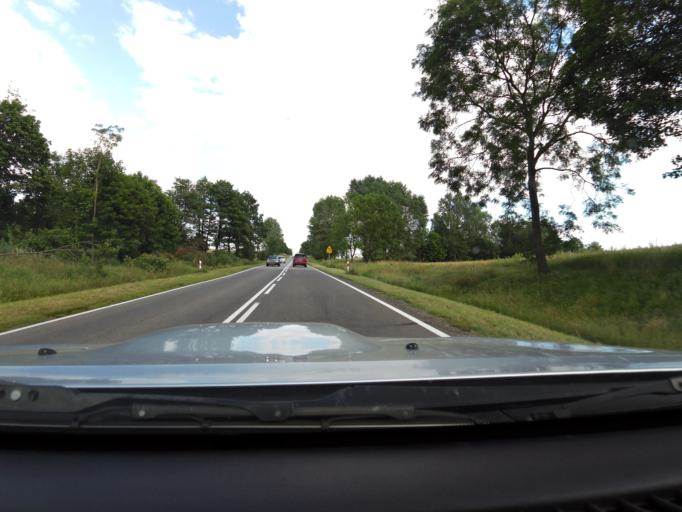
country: PL
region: Podlasie
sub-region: Powiat grajewski
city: Rajgrod
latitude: 53.8624
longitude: 22.6953
